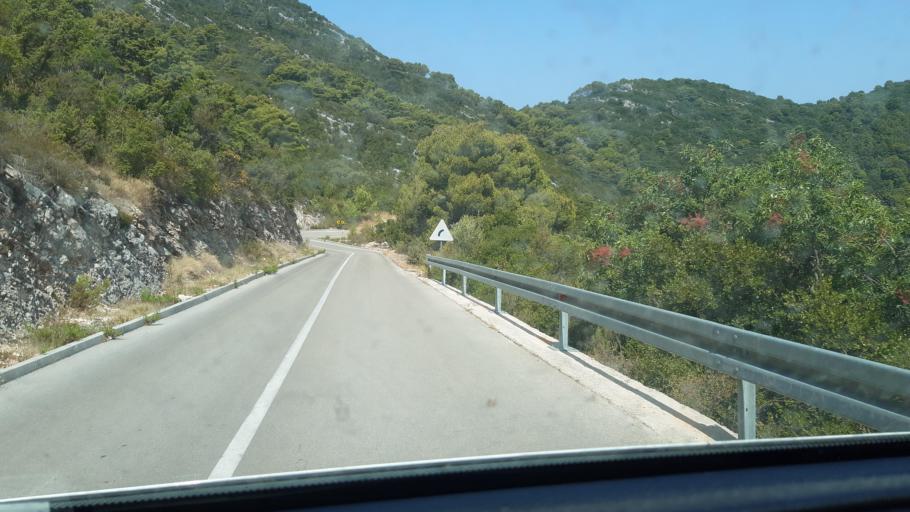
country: HR
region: Dubrovacko-Neretvanska
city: Ston
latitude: 42.7228
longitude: 17.6660
